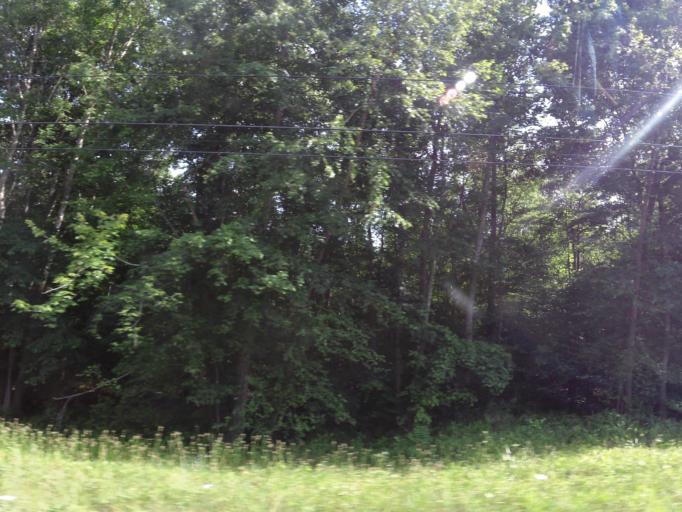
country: US
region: Tennessee
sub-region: Carroll County
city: Bruceton
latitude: 36.0359
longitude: -88.2197
